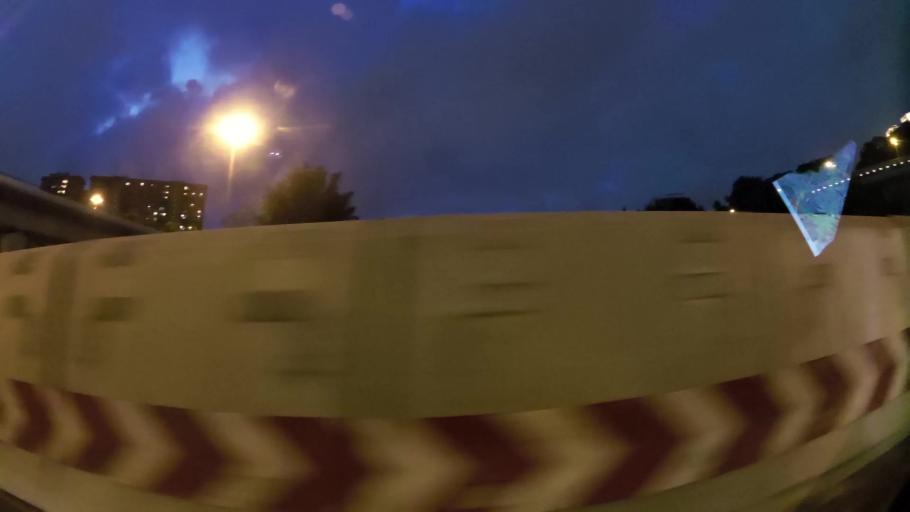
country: HK
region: Kowloon City
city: Kowloon
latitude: 22.3078
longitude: 114.1810
